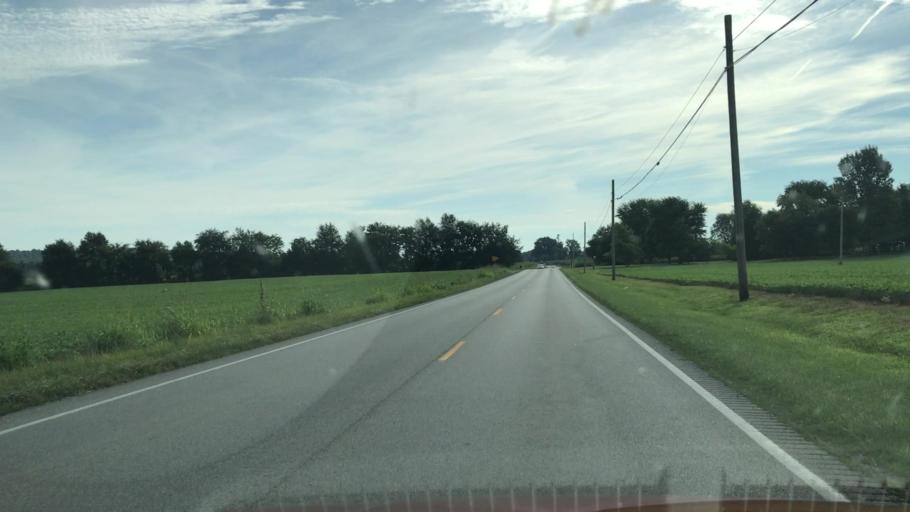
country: US
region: Kentucky
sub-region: Edmonson County
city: Brownsville
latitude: 37.0657
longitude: -86.2796
